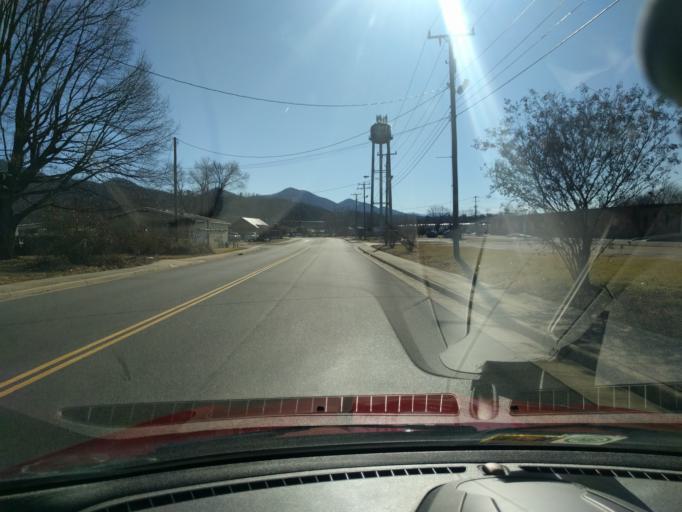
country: US
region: Virginia
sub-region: City of Buena Vista
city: Buena Vista
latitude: 37.7306
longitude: -79.3567
